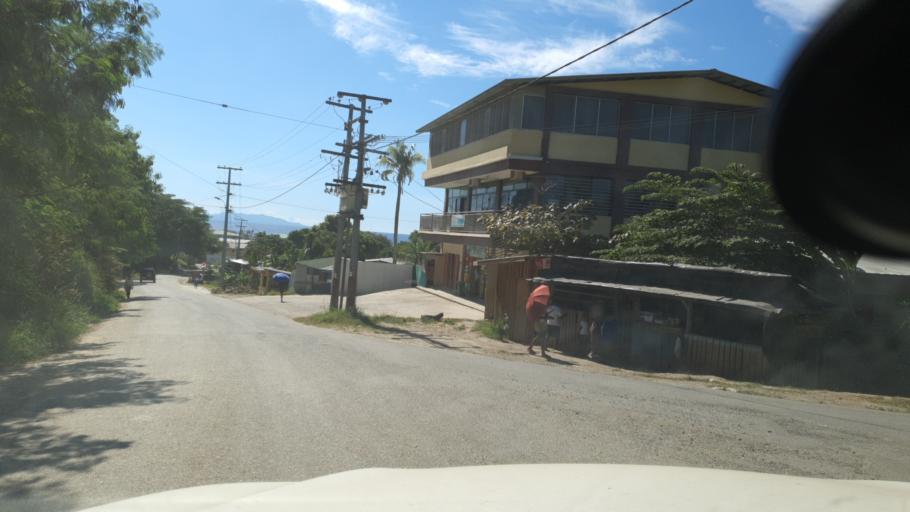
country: SB
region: Guadalcanal
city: Honiara
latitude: -9.4398
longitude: 159.9693
